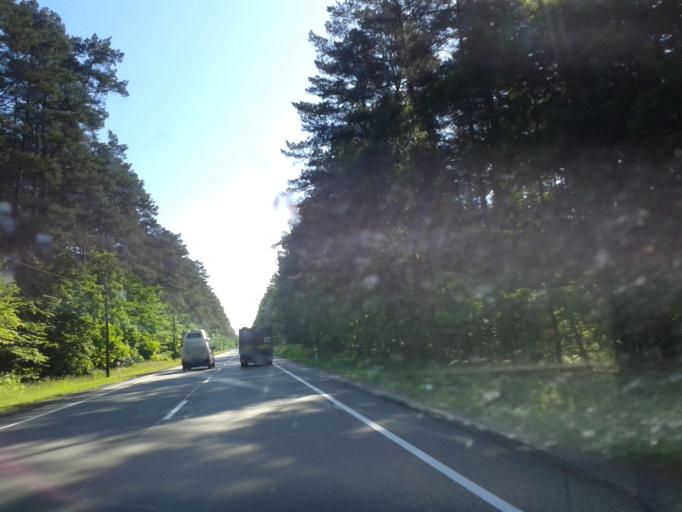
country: PL
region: Pomeranian Voivodeship
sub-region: Powiat chojnicki
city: Czersk
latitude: 53.7866
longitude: 17.9271
